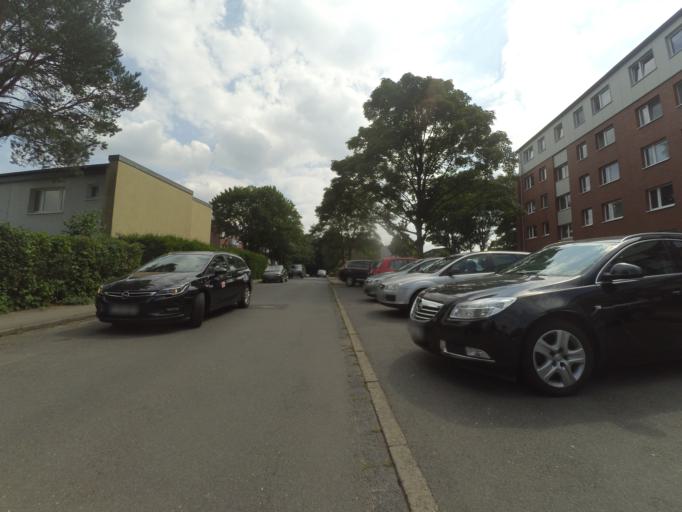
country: DE
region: Hamburg
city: Eidelstedt
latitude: 53.5807
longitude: 9.8708
